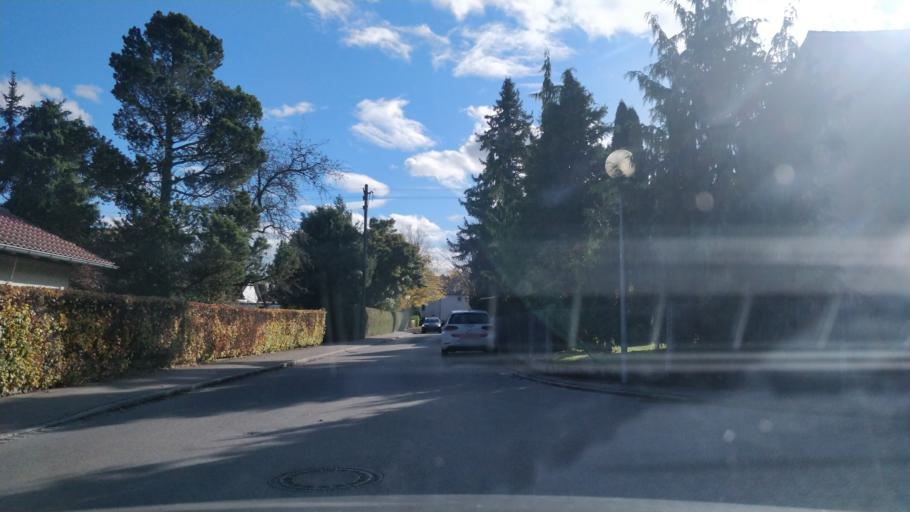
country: DE
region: Bavaria
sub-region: Swabia
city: Mering
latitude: 48.2614
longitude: 10.9776
